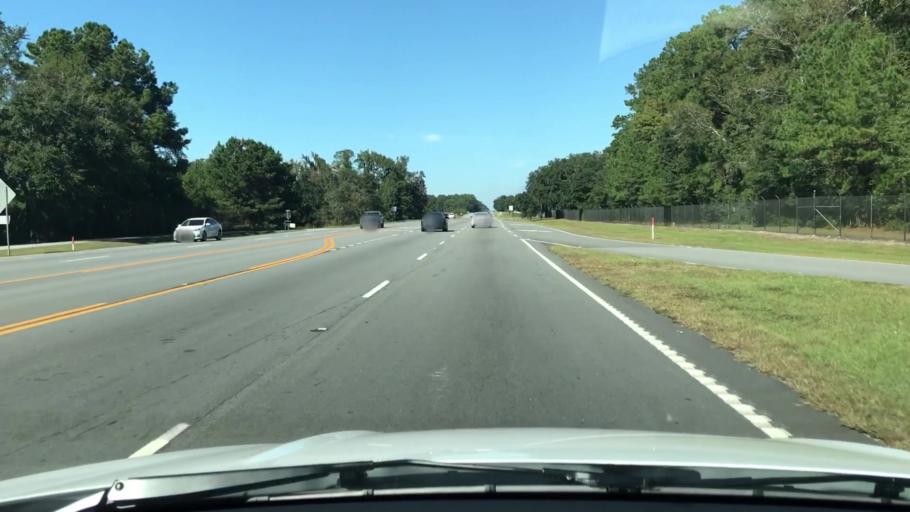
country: US
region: South Carolina
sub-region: Beaufort County
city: Burton
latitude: 32.4604
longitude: -80.7343
